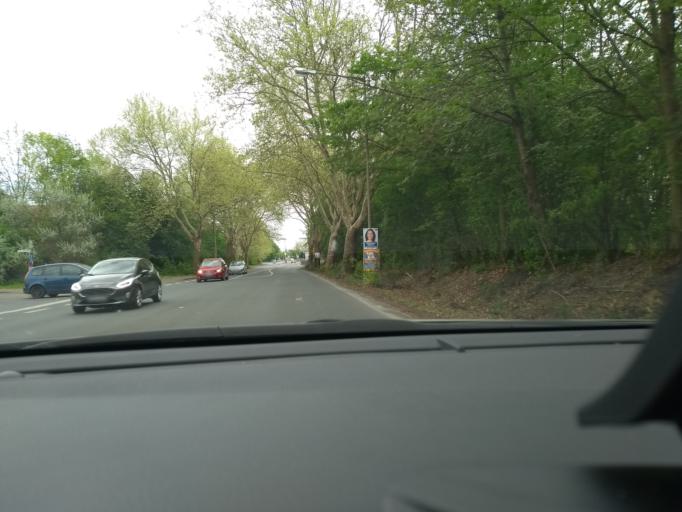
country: DE
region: North Rhine-Westphalia
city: Lunen
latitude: 51.6024
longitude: 7.5234
